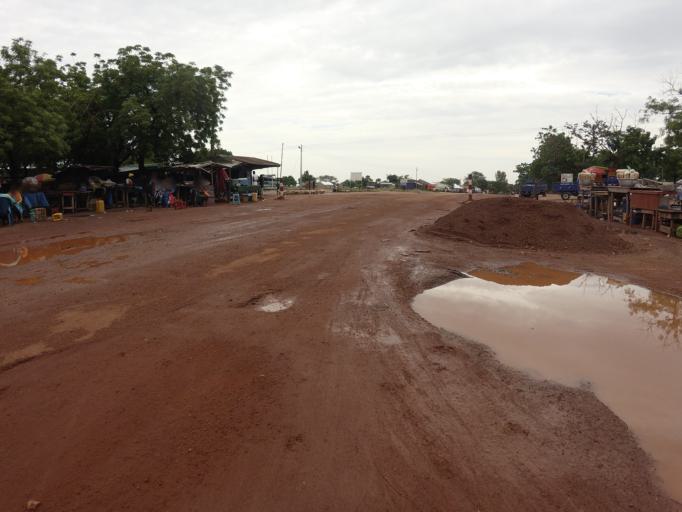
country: GH
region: Upper East
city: Bawku
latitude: 10.9353
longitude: -0.4974
